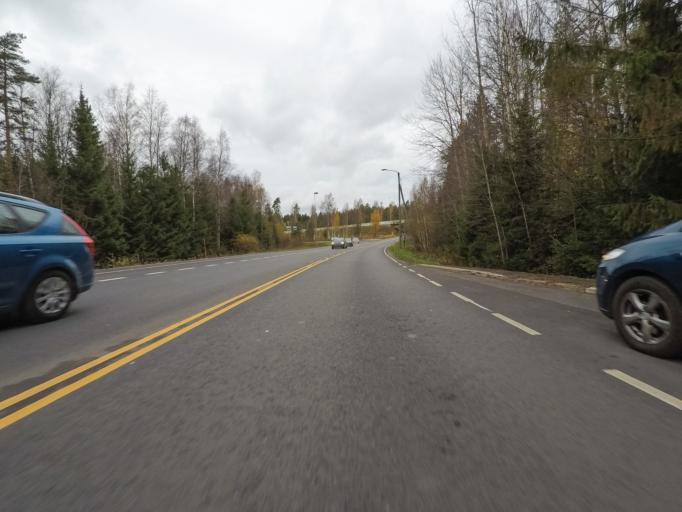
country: FI
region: Uusimaa
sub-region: Porvoo
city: Porvoo
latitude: 60.4150
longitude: 25.6739
